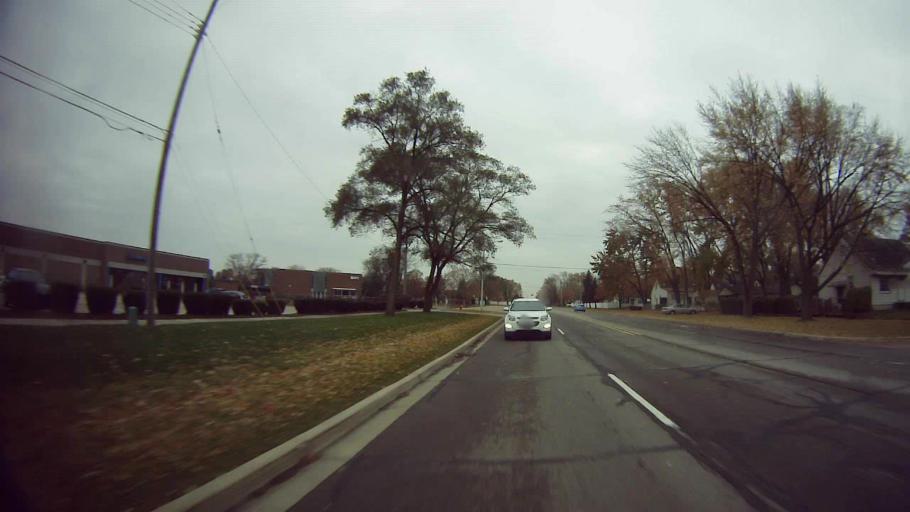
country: US
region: Michigan
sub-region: Oakland County
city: Clawson
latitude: 42.5295
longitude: -83.1260
